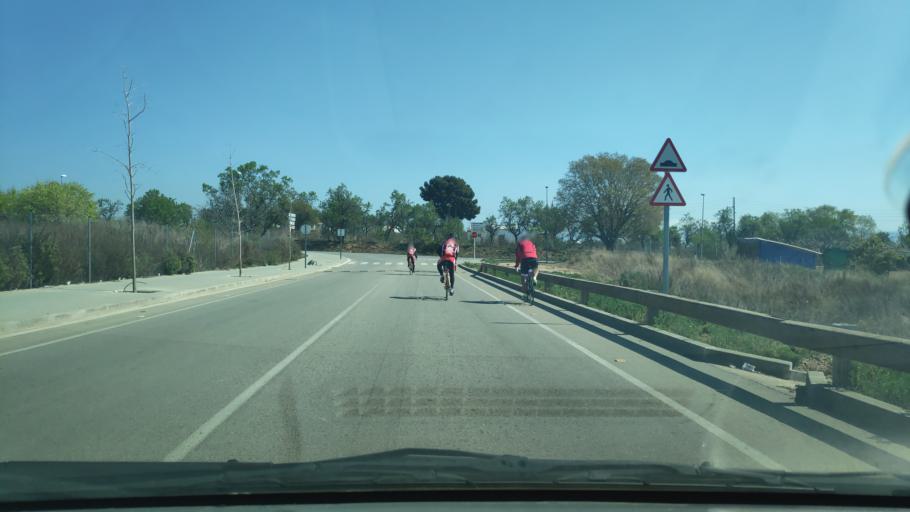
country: ES
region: Catalonia
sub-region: Provincia de Barcelona
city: Sabadell
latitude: 41.5545
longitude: 2.1251
